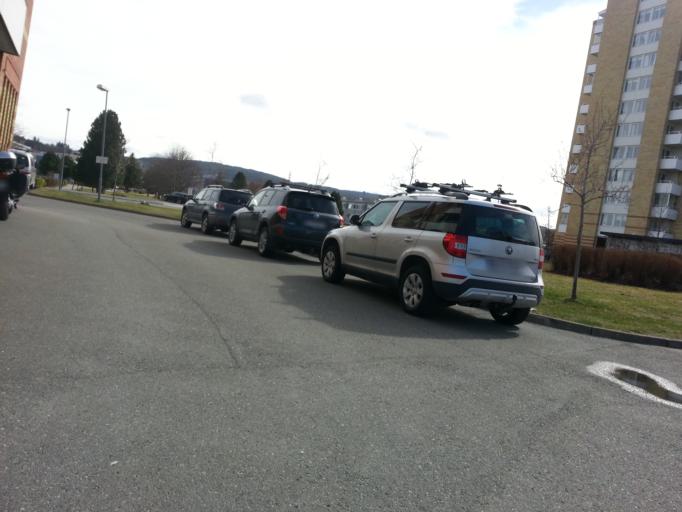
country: NO
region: Sor-Trondelag
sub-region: Trondheim
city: Trondheim
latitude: 63.4232
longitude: 10.4435
